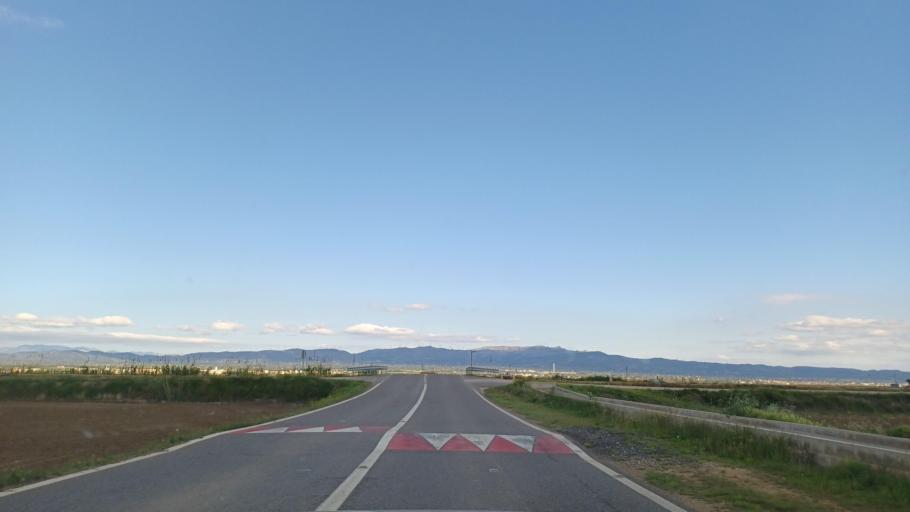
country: ES
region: Catalonia
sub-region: Provincia de Tarragona
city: Deltebre
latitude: 40.7537
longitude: 0.7041
